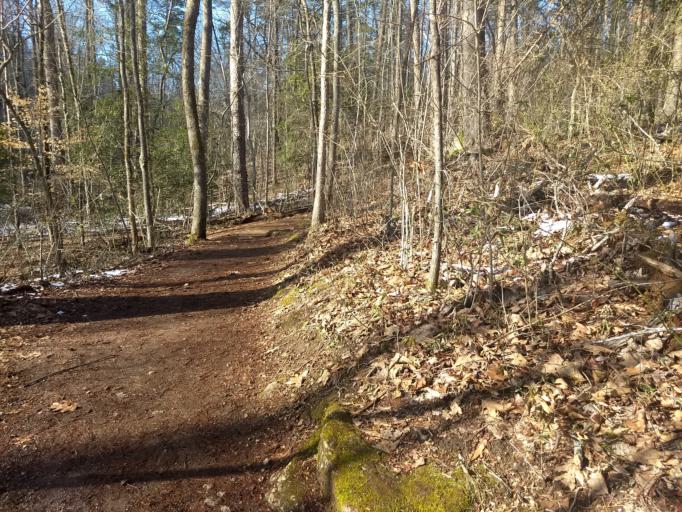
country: US
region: South Carolina
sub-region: Greenville County
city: Wade Hampton
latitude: 34.9268
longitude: -82.3769
